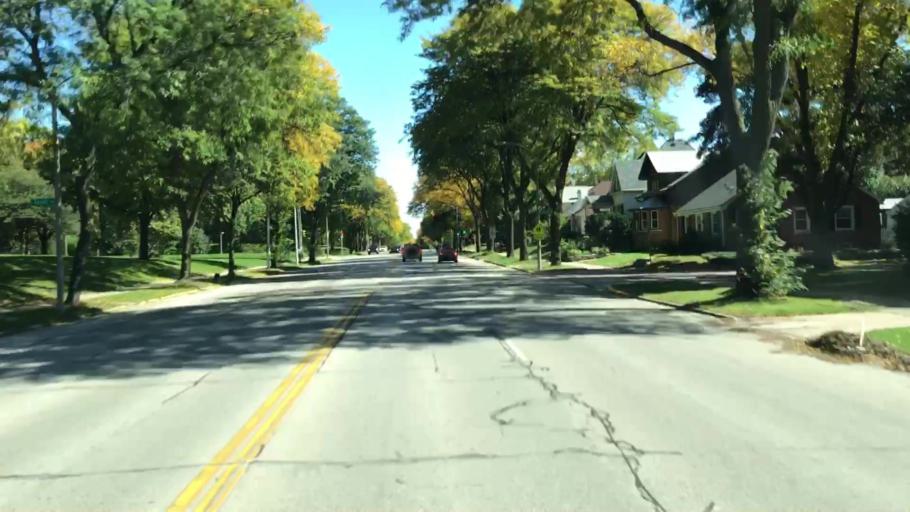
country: US
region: Wisconsin
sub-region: Milwaukee County
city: Saint Francis
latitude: 42.9883
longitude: -87.9010
